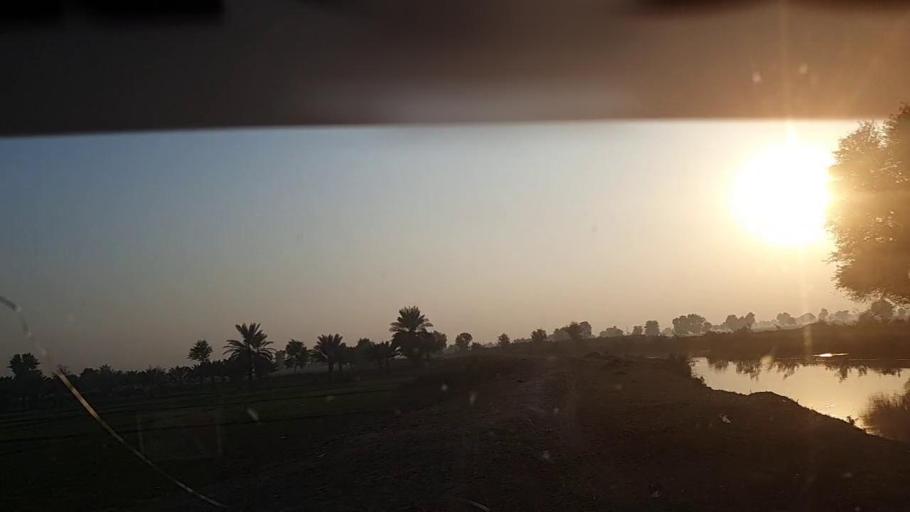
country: PK
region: Sindh
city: Ranipur
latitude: 27.2283
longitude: 68.5447
